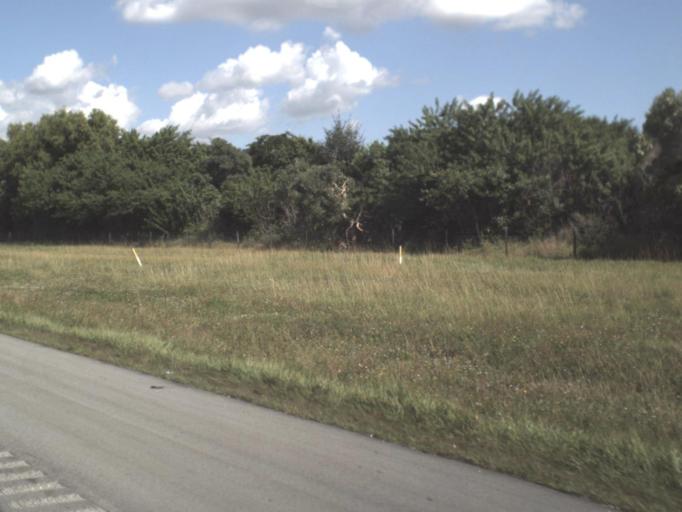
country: US
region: Florida
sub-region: Palm Beach County
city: Villages of Oriole
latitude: 26.4361
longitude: -80.1736
